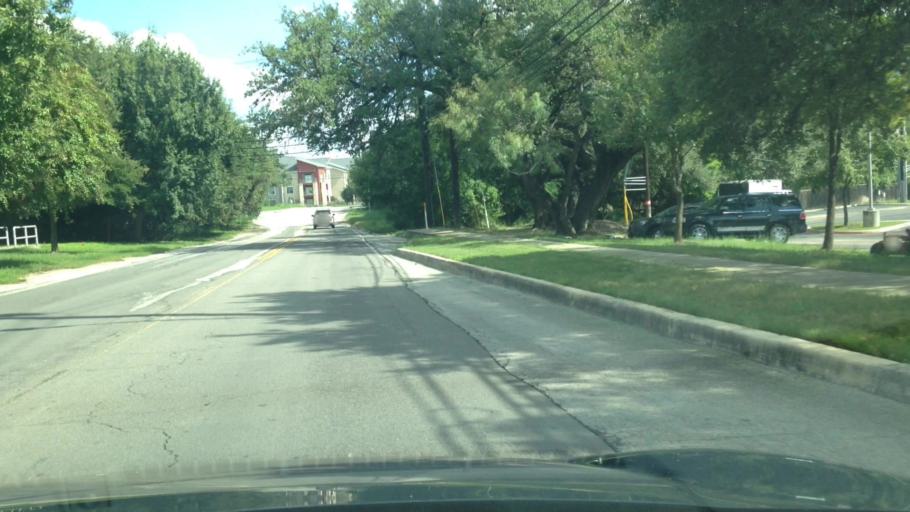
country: US
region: Texas
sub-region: Bexar County
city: Shavano Park
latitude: 29.5445
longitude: -98.5887
